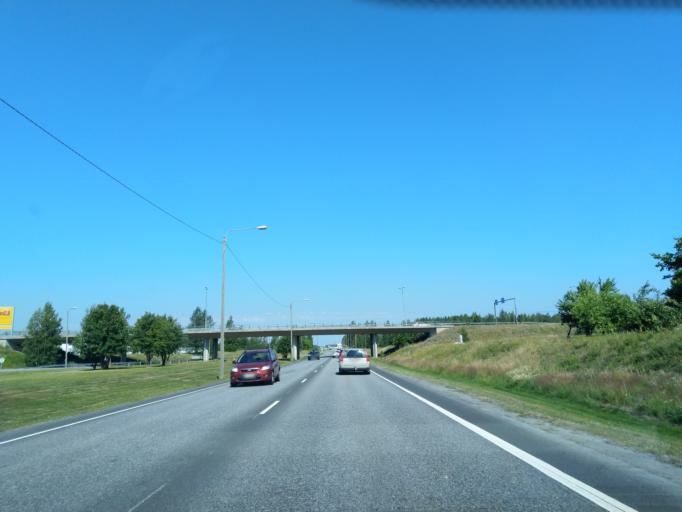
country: FI
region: Satakunta
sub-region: Pori
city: Nakkila
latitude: 61.3610
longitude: 21.9960
